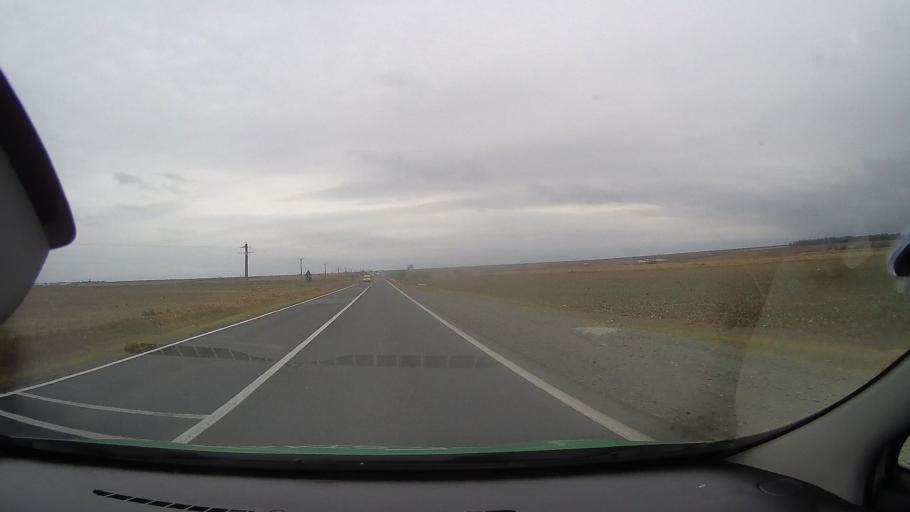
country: RO
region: Constanta
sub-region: Comuna Nicolae Balcescu
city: Nicolae Balcescu
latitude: 44.3870
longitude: 28.3875
